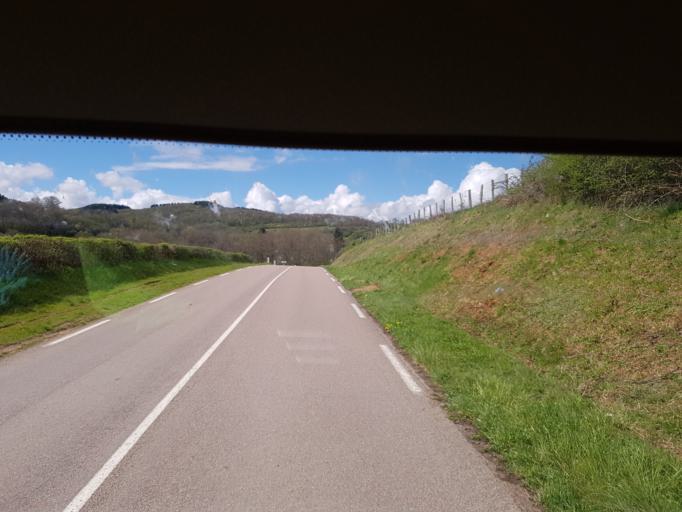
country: FR
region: Bourgogne
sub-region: Departement de Saone-et-Loire
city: Autun
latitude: 47.0968
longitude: 4.2330
